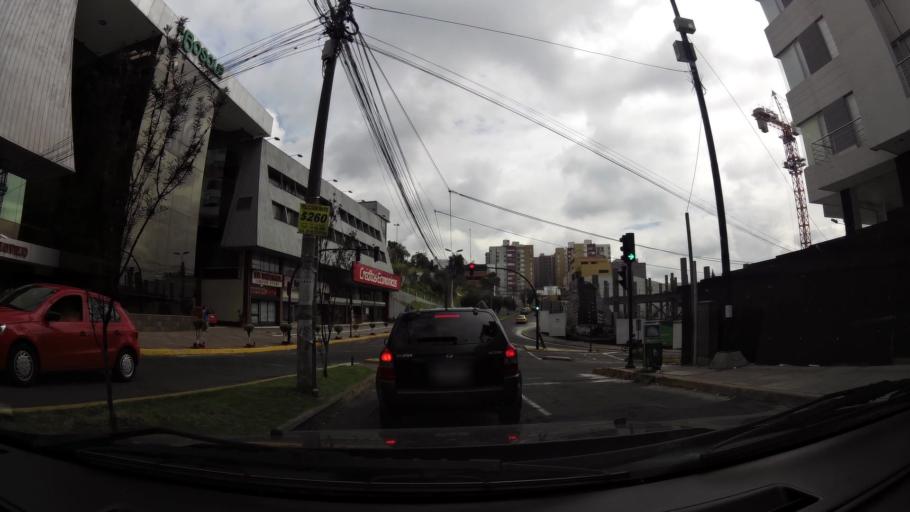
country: EC
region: Pichincha
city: Quito
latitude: -0.1618
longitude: -78.4966
